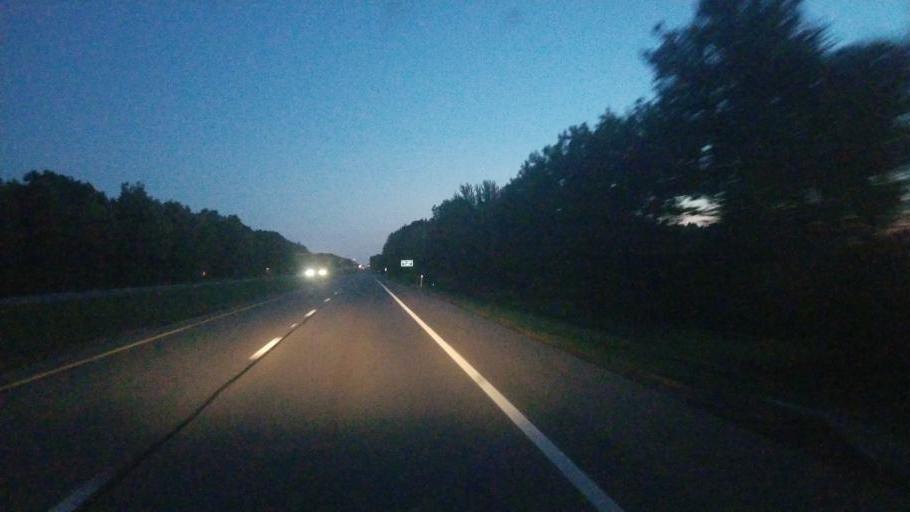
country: US
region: Ohio
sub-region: Ashtabula County
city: Roaming Shores
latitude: 41.5806
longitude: -80.7136
